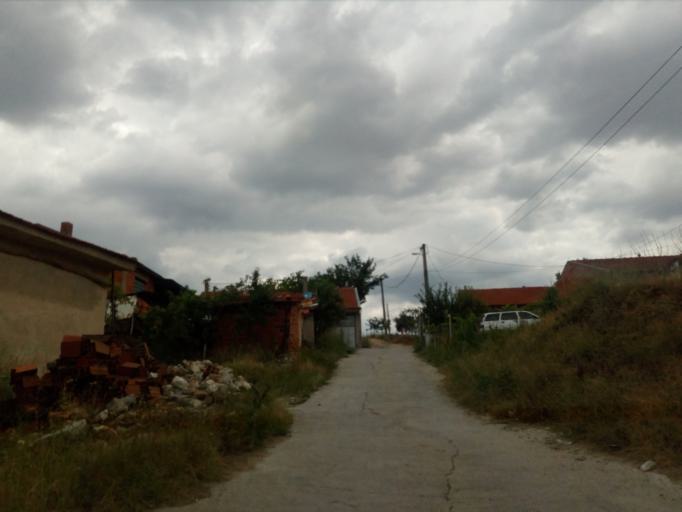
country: MK
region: Veles
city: Veles
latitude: 41.7095
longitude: 21.7588
